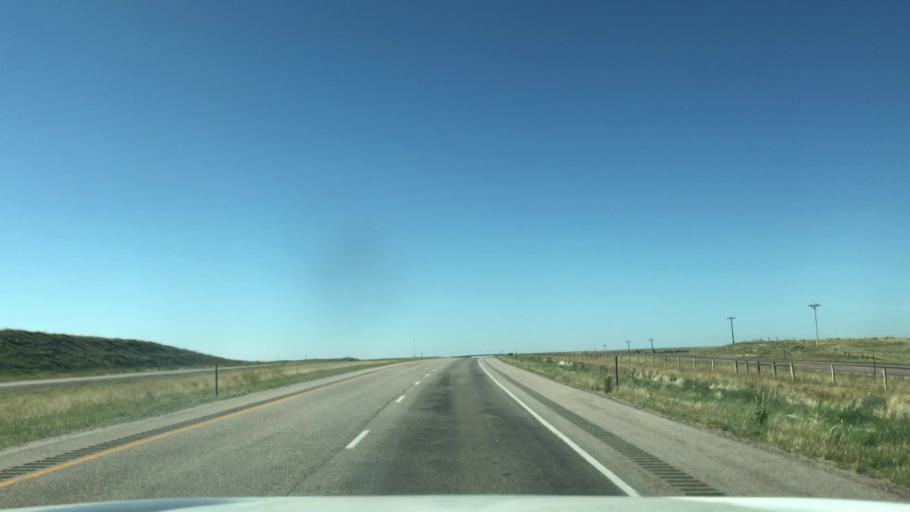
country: US
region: Wyoming
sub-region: Platte County
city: Wheatland
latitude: 41.6834
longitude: -104.8325
